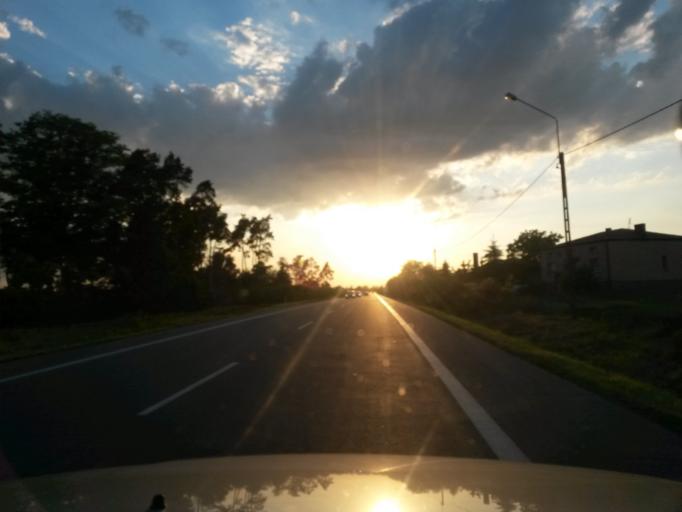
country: PL
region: Lodz Voivodeship
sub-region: Powiat wielunski
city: Czarnozyly
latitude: 51.2523
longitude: 18.5066
